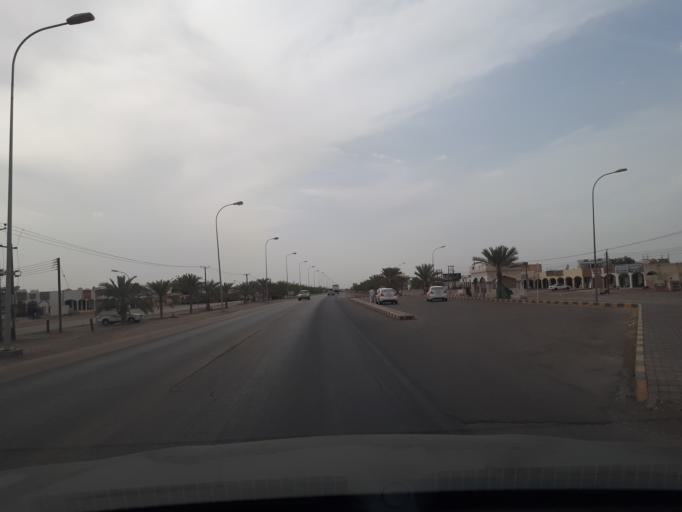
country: OM
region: Ash Sharqiyah
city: Badiyah
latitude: 22.4552
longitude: 58.8056
